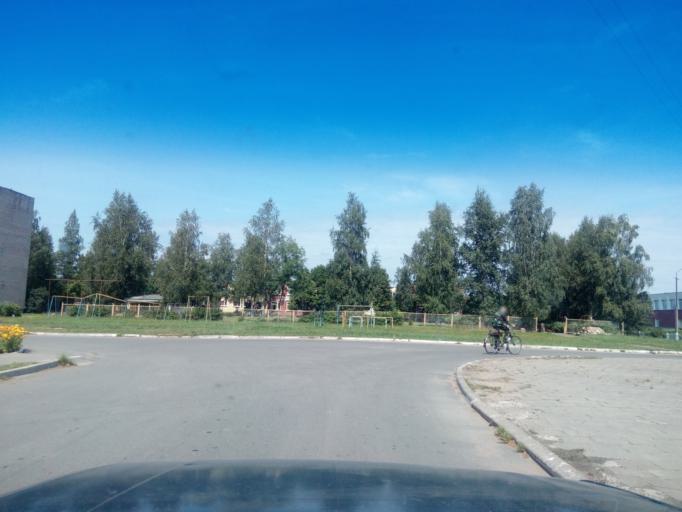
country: BY
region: Vitebsk
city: Vyerkhnyadzvinsk
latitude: 55.8381
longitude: 27.7393
